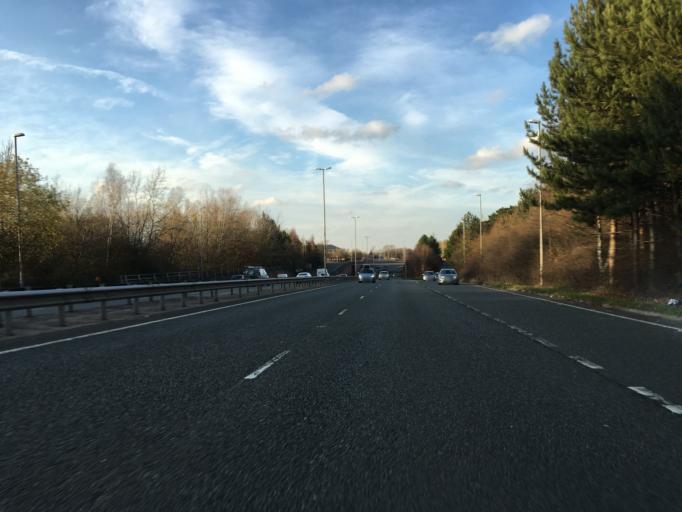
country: GB
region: England
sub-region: Borough of Stockport
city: Cheadle Hulme
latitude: 53.3782
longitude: -2.2150
